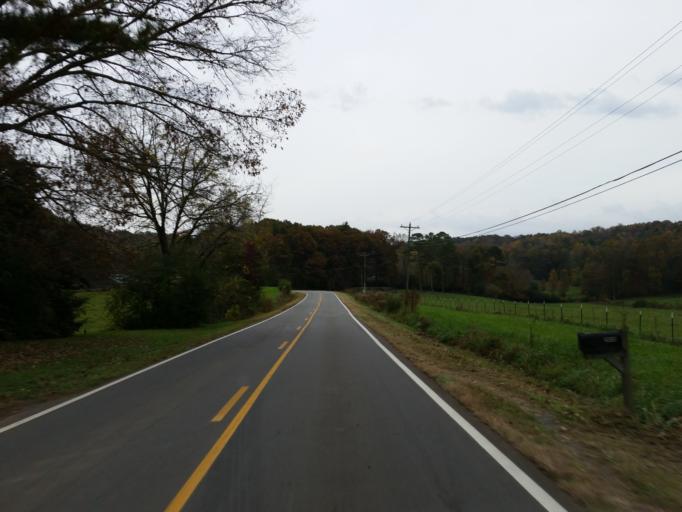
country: US
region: Georgia
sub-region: Gilmer County
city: Ellijay
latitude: 34.6569
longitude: -84.3591
